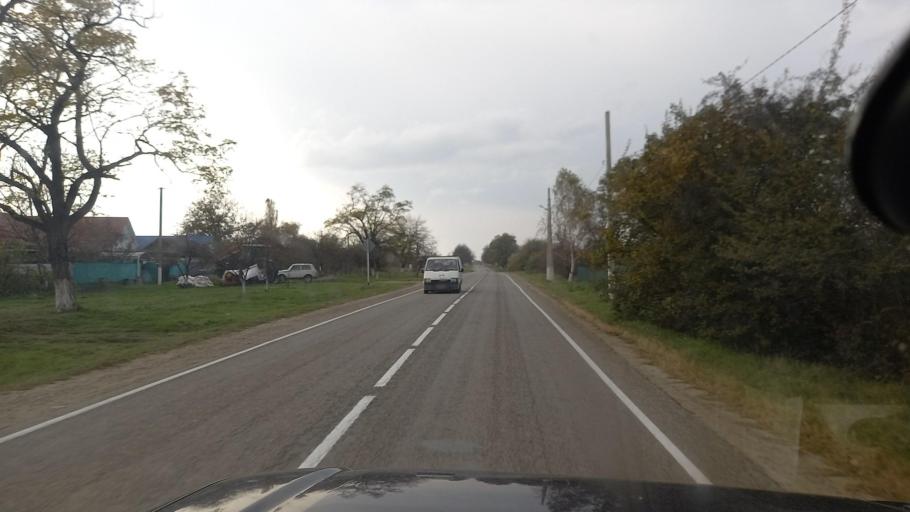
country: RU
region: Krasnodarskiy
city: Gubskaya
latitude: 44.3183
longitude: 40.6195
